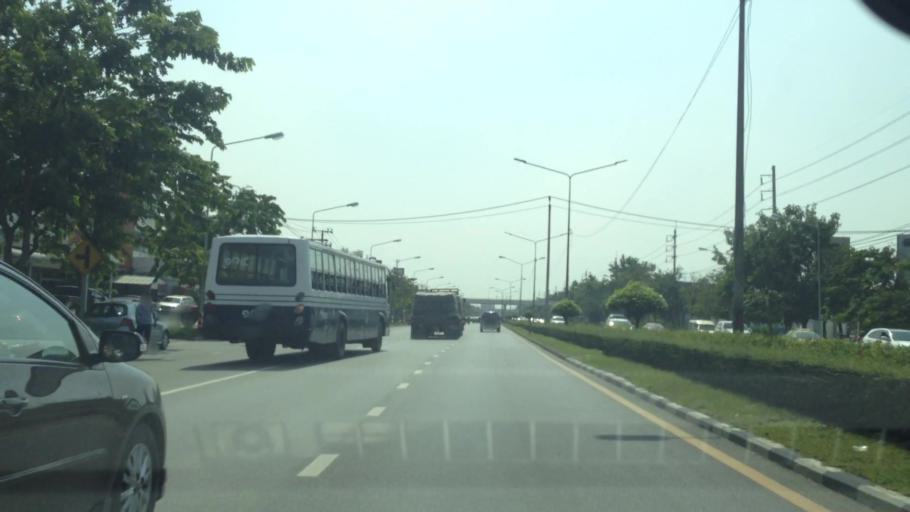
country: TH
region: Bangkok
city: Sai Mai
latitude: 13.9427
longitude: 100.6238
